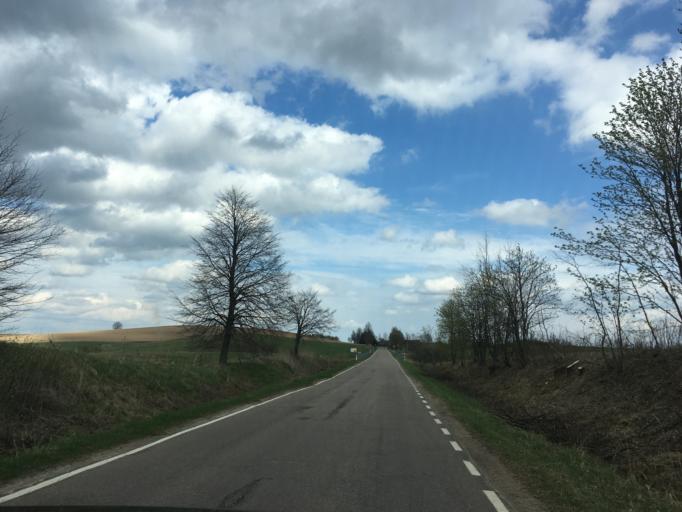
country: LT
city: Virbalis
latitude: 54.3648
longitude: 22.8374
